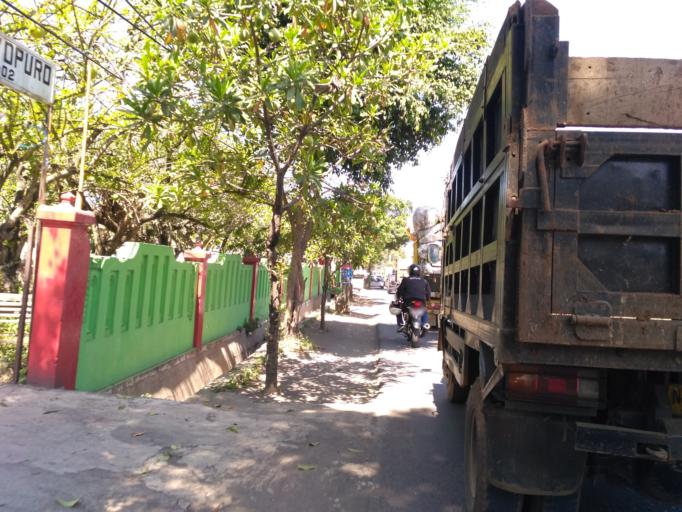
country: ID
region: East Java
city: Malang
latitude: -7.9721
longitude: 112.6732
